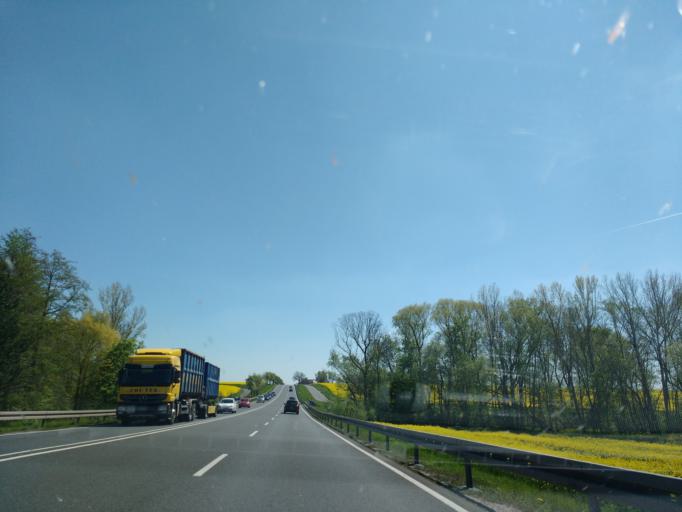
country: DE
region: Saxony-Anhalt
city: Nessa
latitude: 51.1529
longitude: 12.0308
